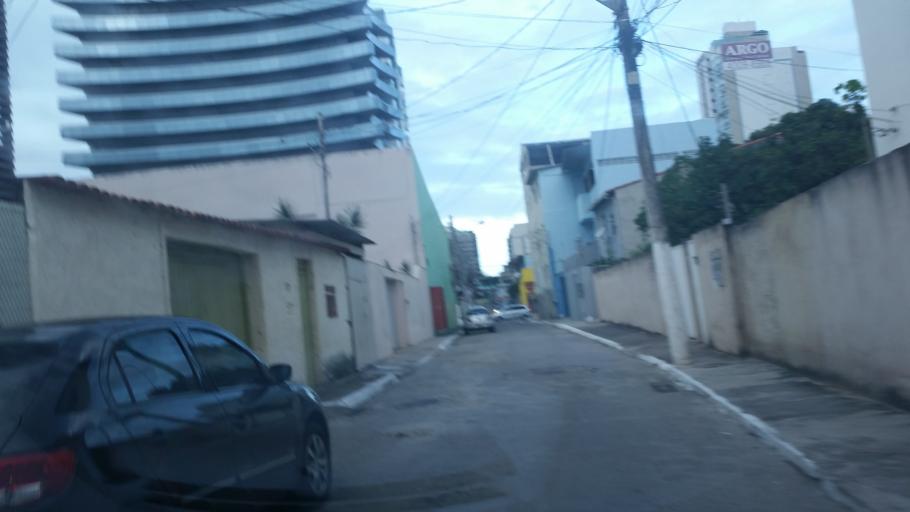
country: BR
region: Espirito Santo
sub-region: Vila Velha
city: Vila Velha
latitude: -20.3388
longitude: -40.2884
